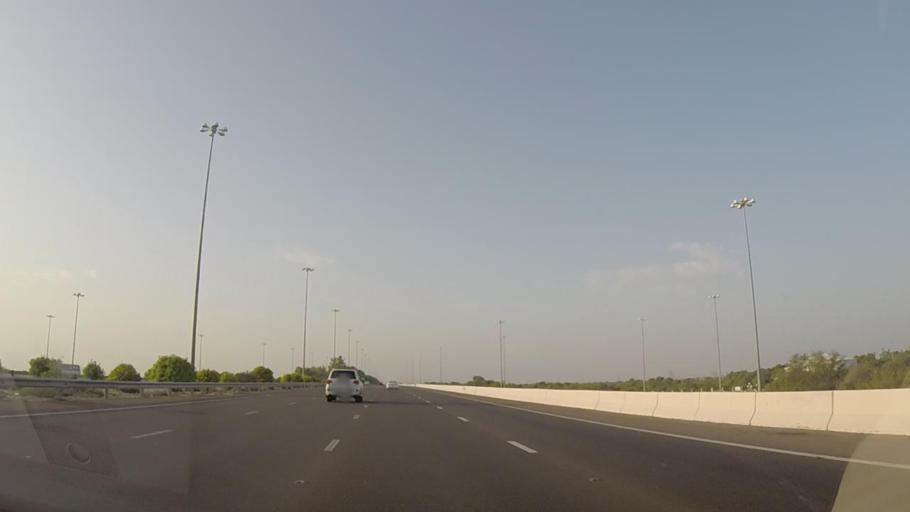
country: AE
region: Dubai
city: Dubai
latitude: 24.7996
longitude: 54.8636
